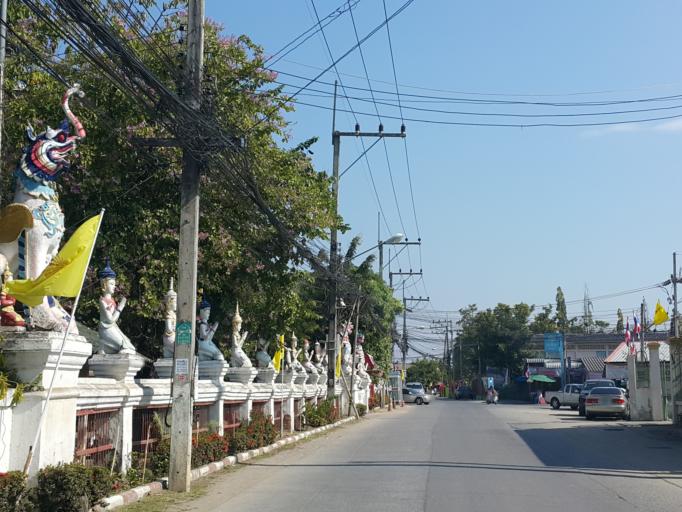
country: TH
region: Chiang Mai
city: San Sai
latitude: 18.8473
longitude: 99.0201
